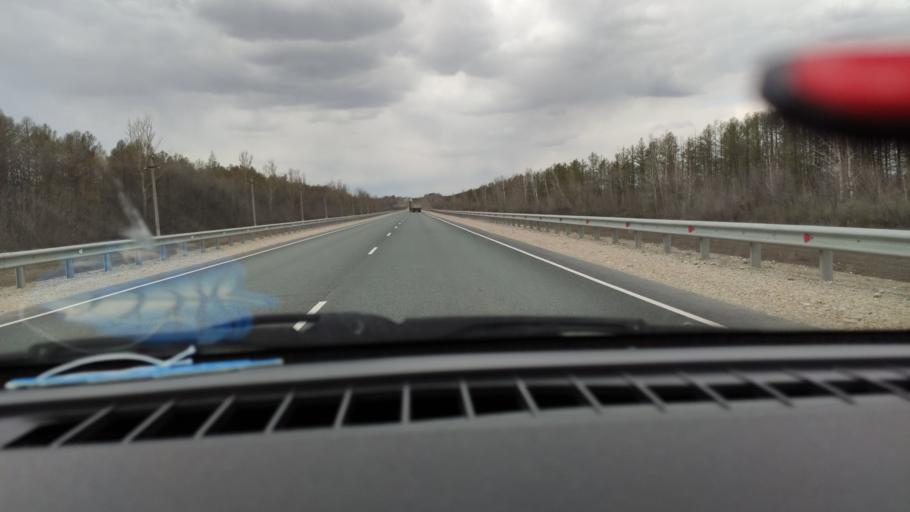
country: RU
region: Saratov
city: Shikhany
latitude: 52.1615
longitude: 47.1389
